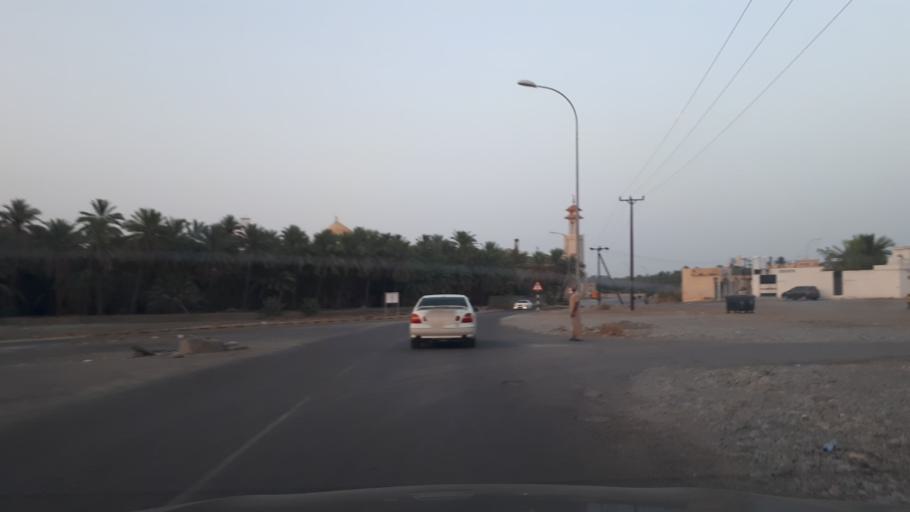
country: OM
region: Al Batinah
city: Rustaq
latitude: 23.5602
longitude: 57.5599
